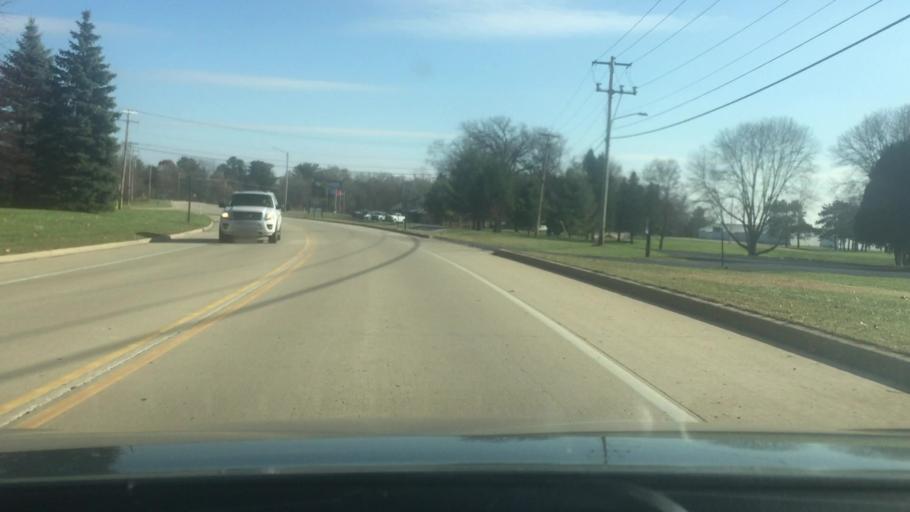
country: US
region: Wisconsin
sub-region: Jefferson County
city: Cambridge
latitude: 43.0003
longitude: -89.0069
